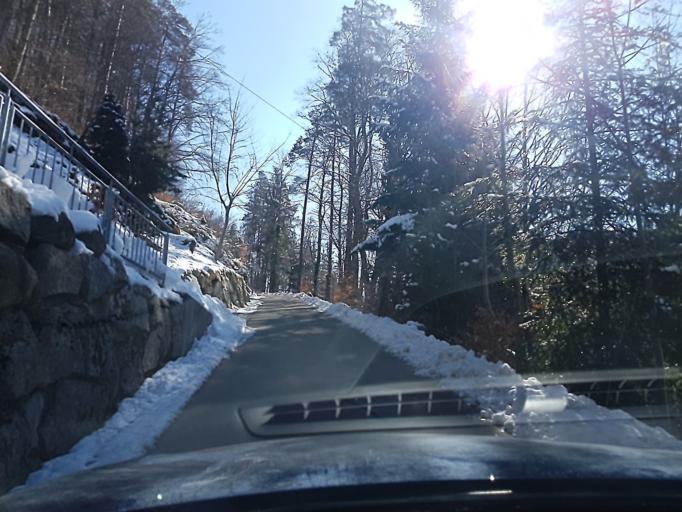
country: DE
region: Baden-Wuerttemberg
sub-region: Freiburg Region
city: Triberg im Schwarzwald
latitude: 48.1384
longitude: 8.2427
